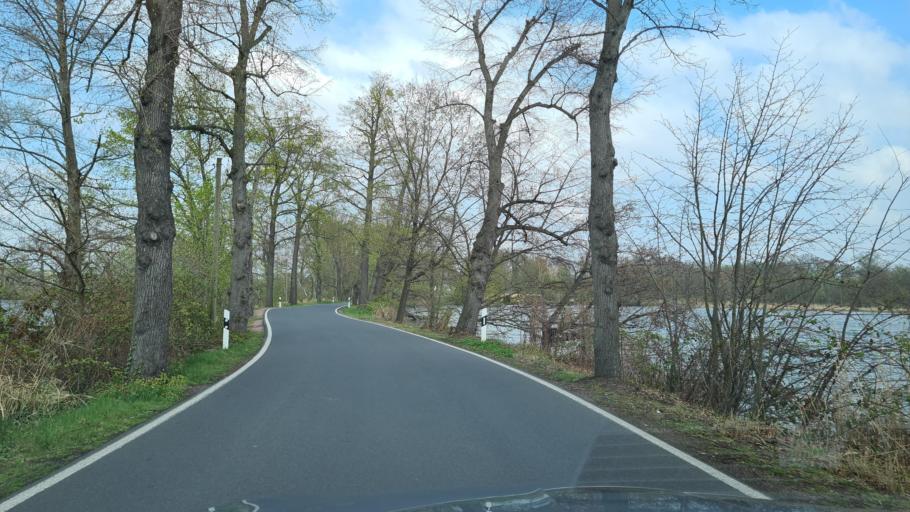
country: DE
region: Saxony
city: Wulknitz
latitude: 51.3830
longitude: 13.4280
